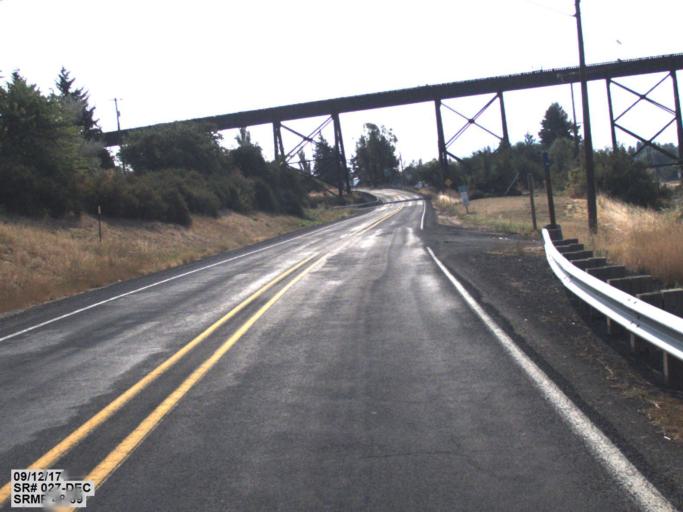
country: US
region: Idaho
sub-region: Benewah County
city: Plummer
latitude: 47.2281
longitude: -117.0805
